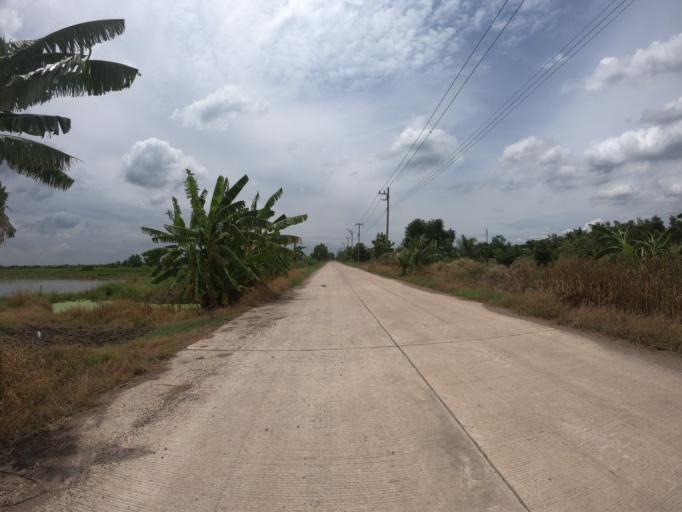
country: TH
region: Pathum Thani
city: Ban Lam Luk Ka
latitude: 14.0202
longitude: 100.8654
